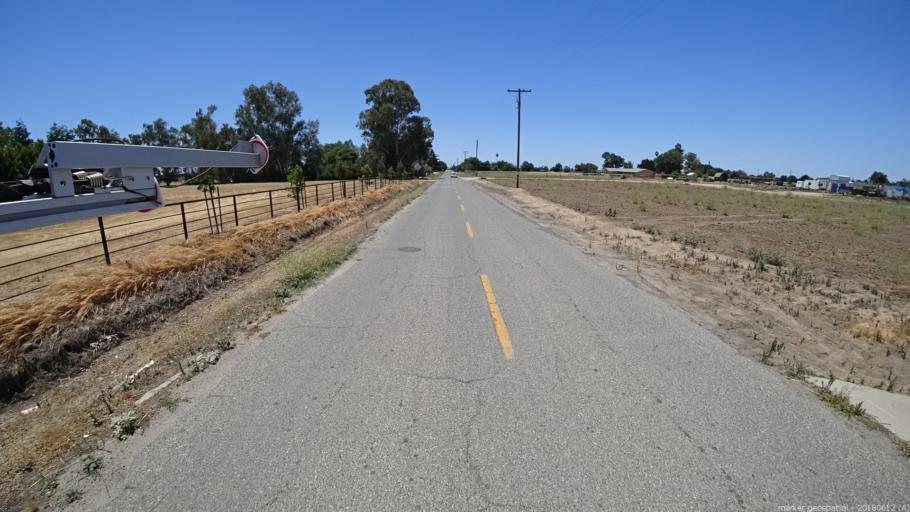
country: US
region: California
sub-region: Madera County
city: Chowchilla
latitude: 37.0910
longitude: -120.2579
